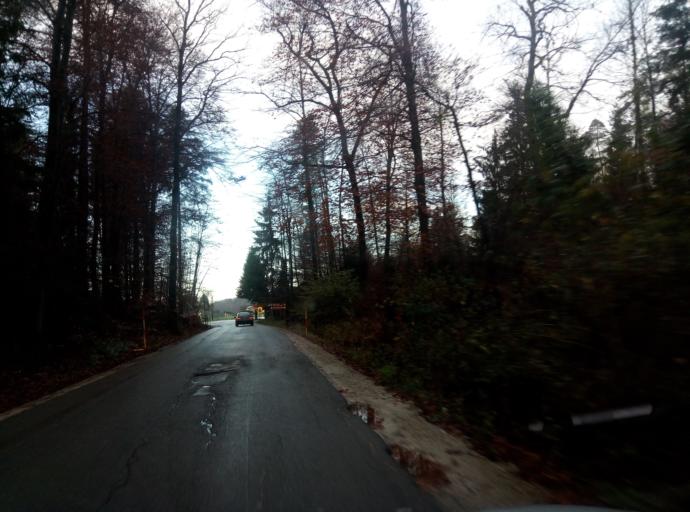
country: SI
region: Komenda
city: Moste
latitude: 46.1679
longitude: 14.5395
